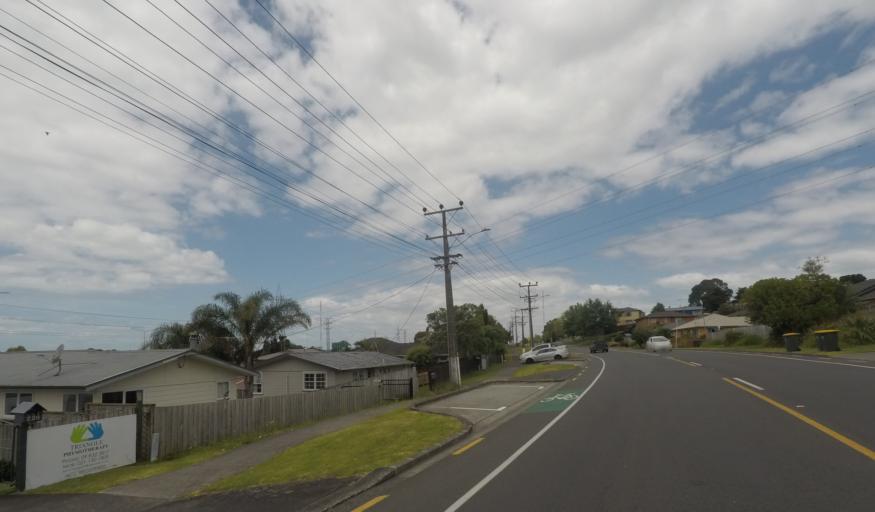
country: NZ
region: Auckland
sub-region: Auckland
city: Rosebank
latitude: -36.8414
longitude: 174.6213
